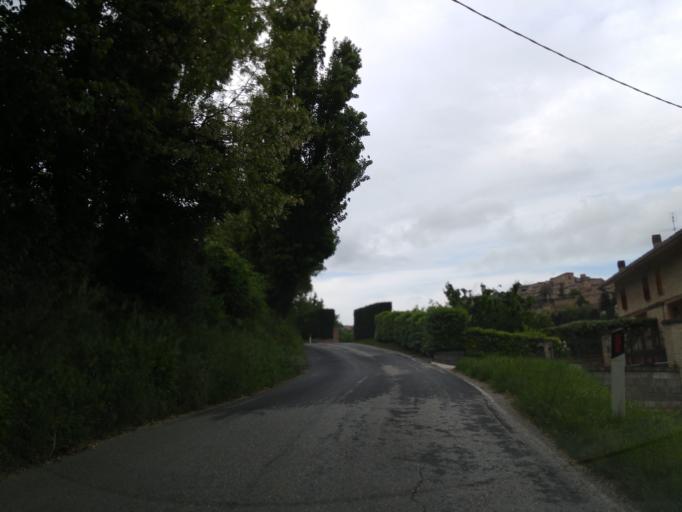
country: IT
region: The Marches
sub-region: Provincia di Pesaro e Urbino
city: Urbino
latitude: 43.7167
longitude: 12.6318
